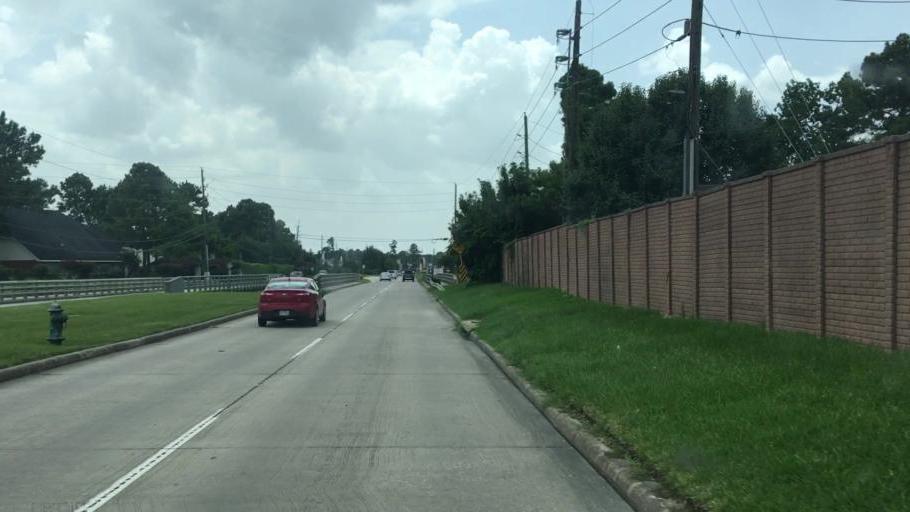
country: US
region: Texas
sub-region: Harris County
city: Atascocita
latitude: 29.9896
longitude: -95.1617
